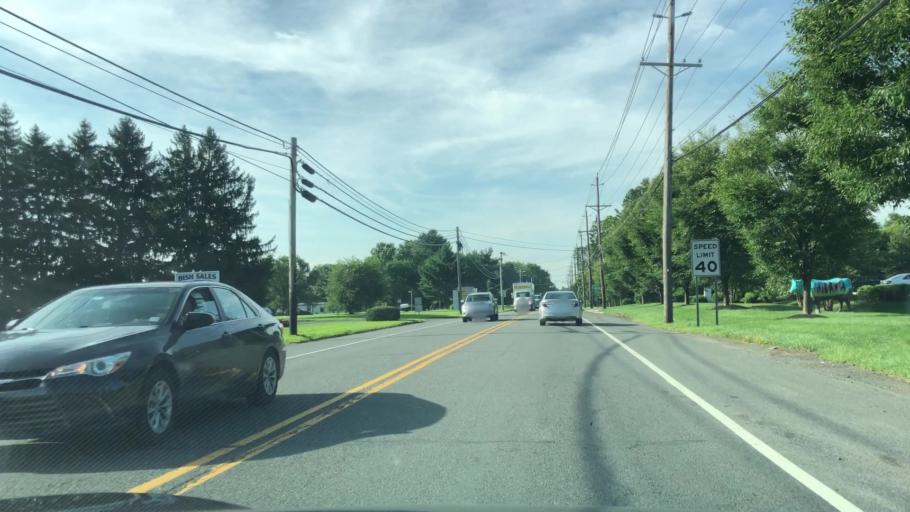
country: US
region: New Jersey
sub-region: Mercer County
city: Pennington
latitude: 40.3468
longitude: -74.7967
